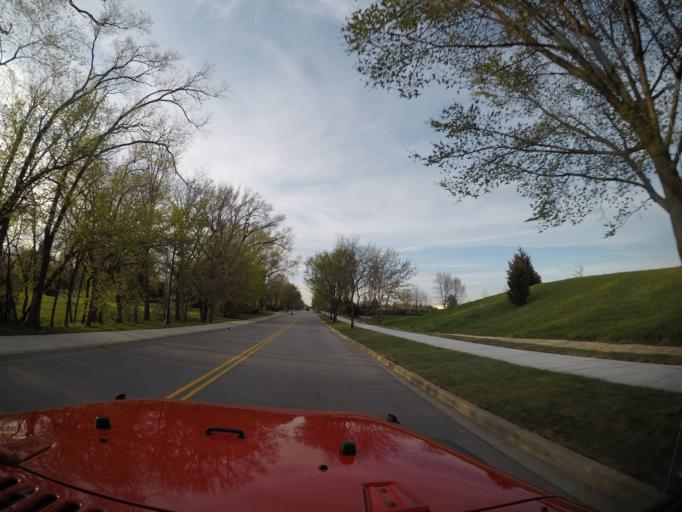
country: US
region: Illinois
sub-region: Cook County
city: Northbrook
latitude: 42.0958
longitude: -87.8295
